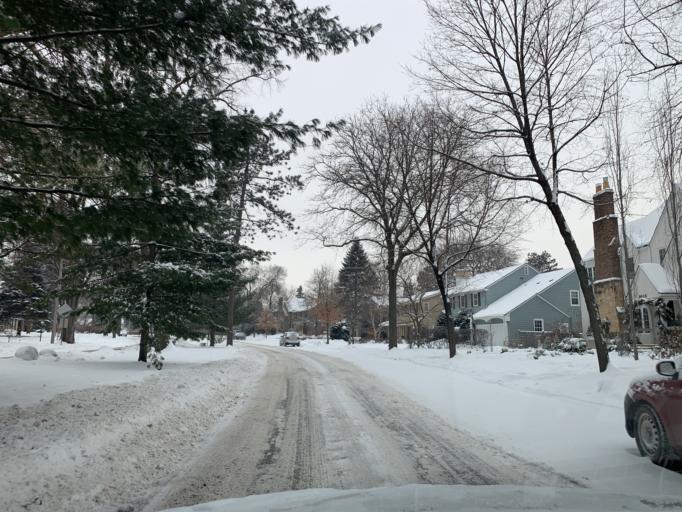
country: US
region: Minnesota
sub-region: Hennepin County
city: Saint Louis Park
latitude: 44.9509
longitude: -93.3270
